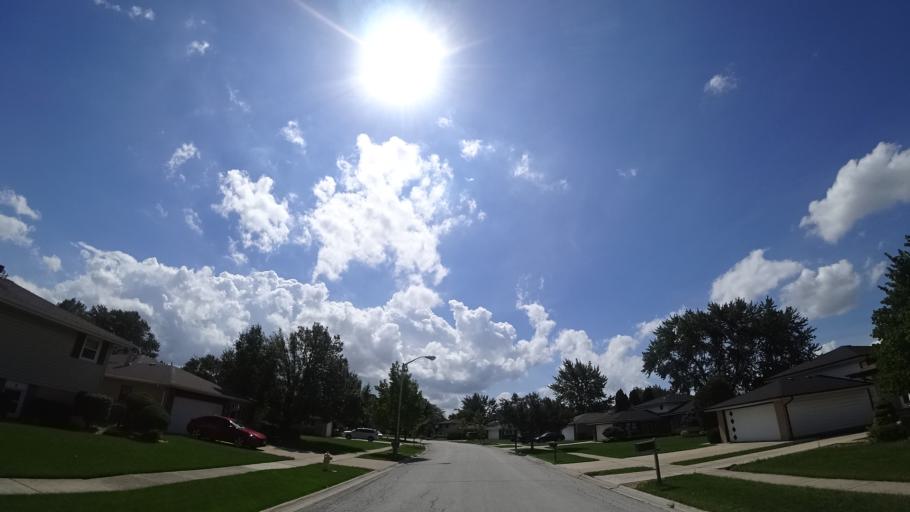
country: US
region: Illinois
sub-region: Cook County
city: Tinley Park
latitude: 41.5653
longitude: -87.7788
